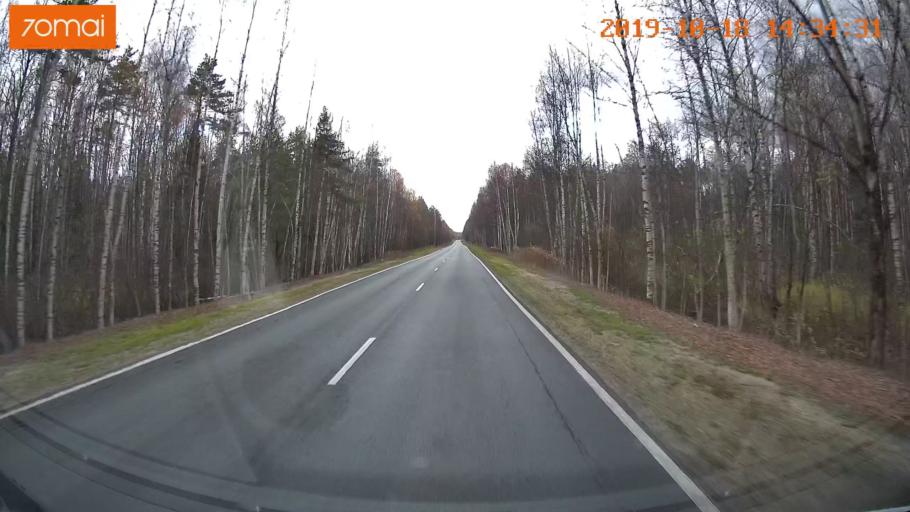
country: RU
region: Vladimir
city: Velikodvorskiy
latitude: 55.2131
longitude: 40.6178
